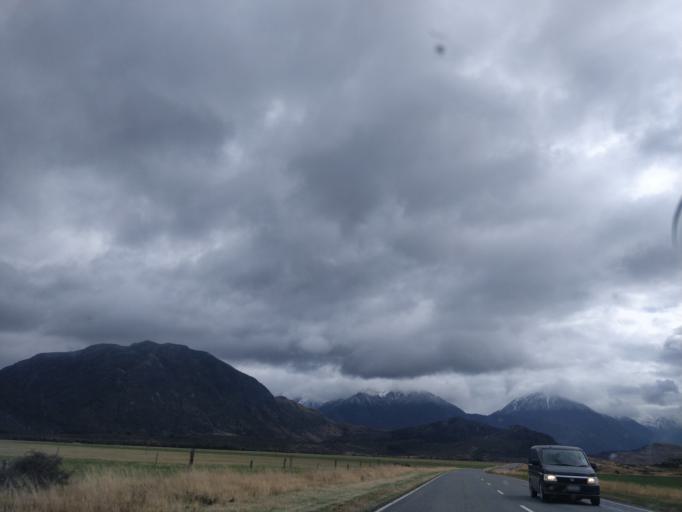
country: NZ
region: Canterbury
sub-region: Waimakariri District
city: Oxford
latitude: -43.0474
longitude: 171.7541
